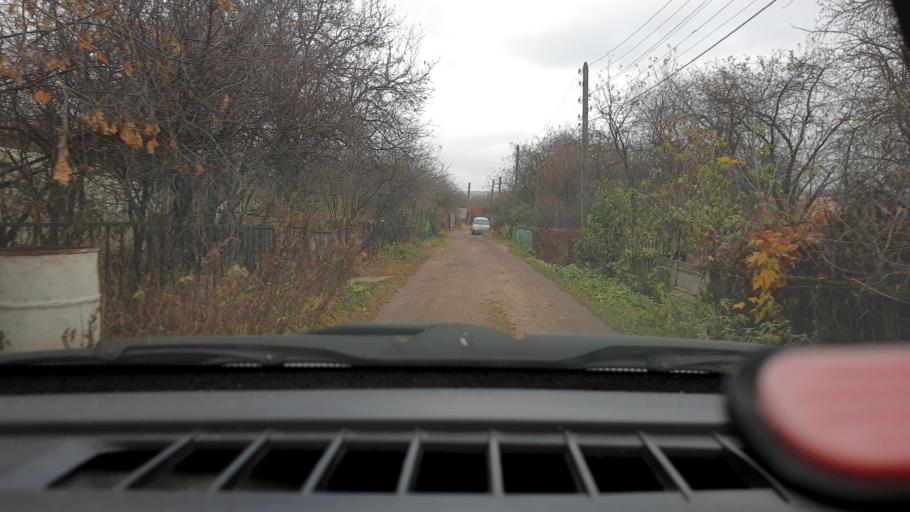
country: RU
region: Nizjnij Novgorod
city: Nizhniy Novgorod
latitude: 56.2599
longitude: 43.9448
